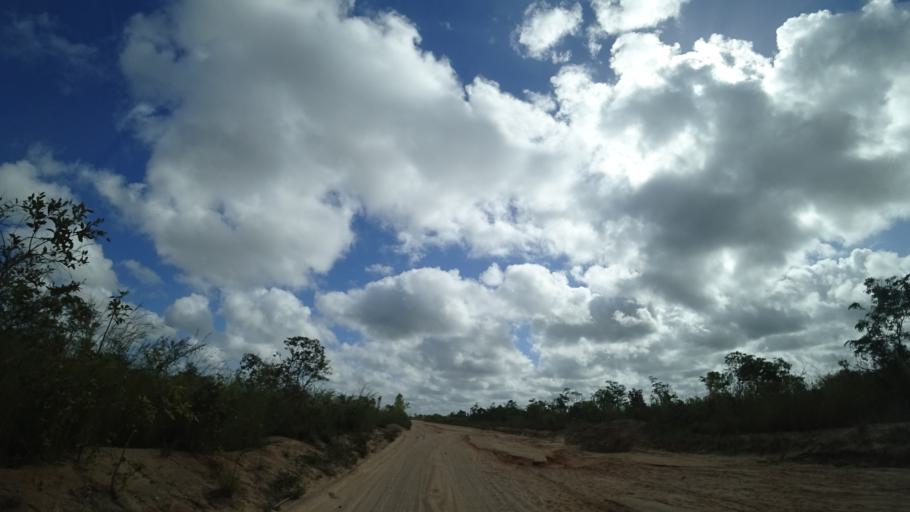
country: MZ
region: Sofala
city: Dondo
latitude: -19.4570
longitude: 34.7188
